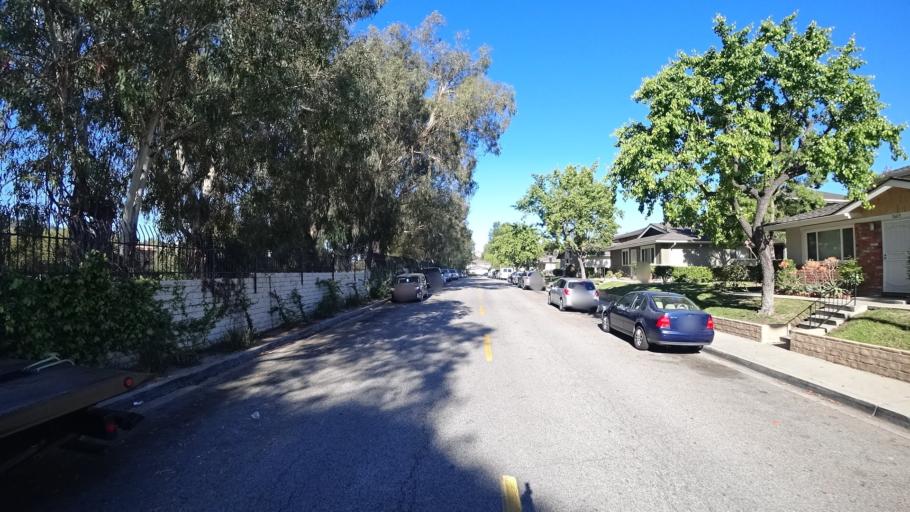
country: US
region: California
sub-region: Ventura County
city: Casa Conejo
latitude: 34.1849
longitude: -118.9147
